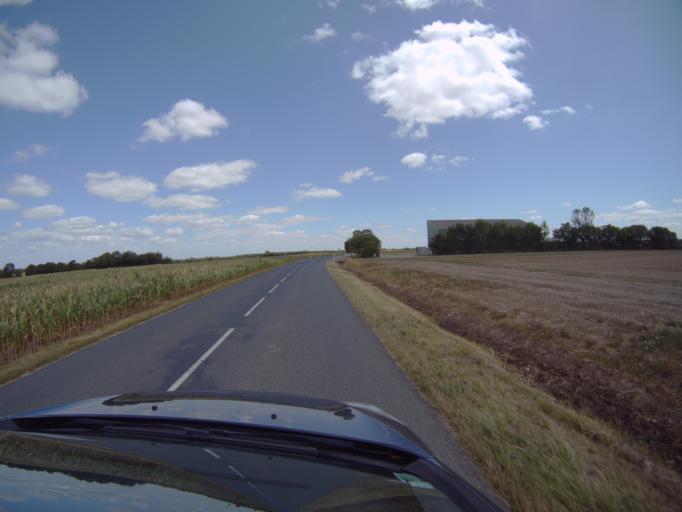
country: FR
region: Poitou-Charentes
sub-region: Departement de la Charente-Maritime
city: Saint-Jean-de-Liversay
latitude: 46.2615
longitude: -0.8657
